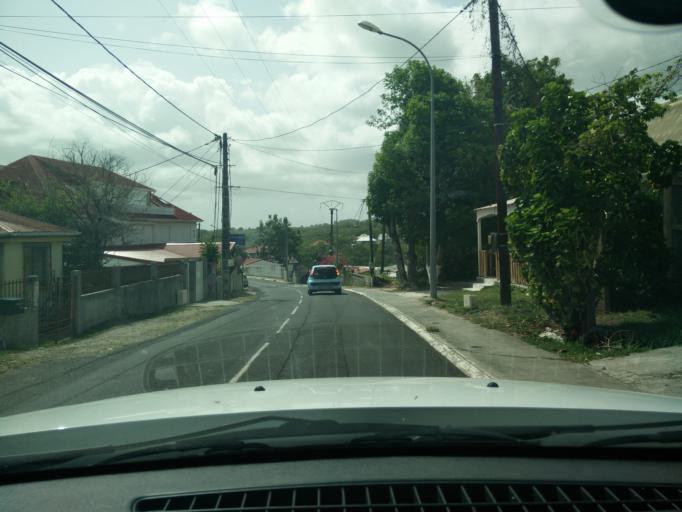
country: GP
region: Guadeloupe
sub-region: Guadeloupe
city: Le Gosier
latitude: 16.2155
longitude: -61.4395
